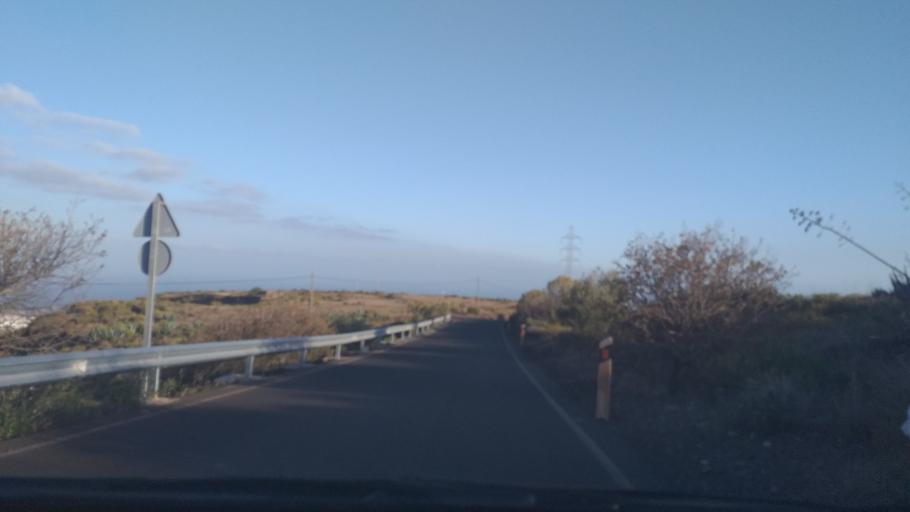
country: ES
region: Canary Islands
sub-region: Provincia de Las Palmas
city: Ingenio
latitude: 27.9264
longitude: -15.4565
